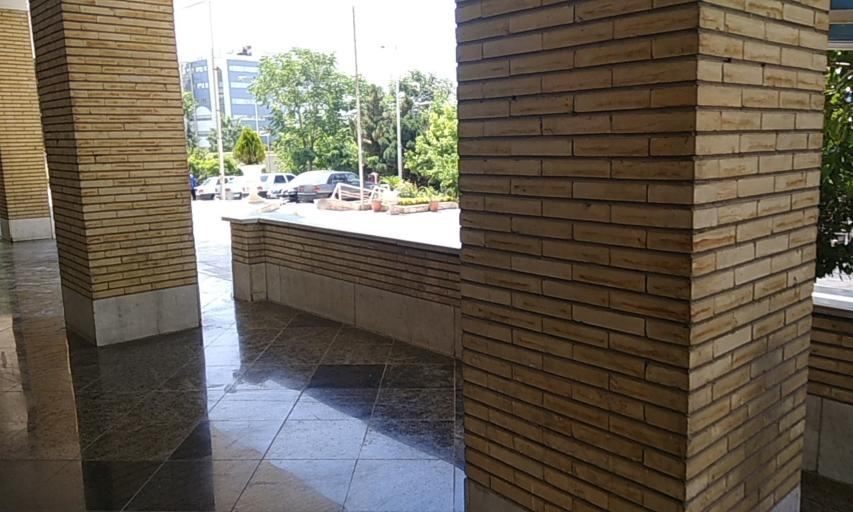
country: IR
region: Tehran
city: Tajrish
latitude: 35.7692
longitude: 51.4087
